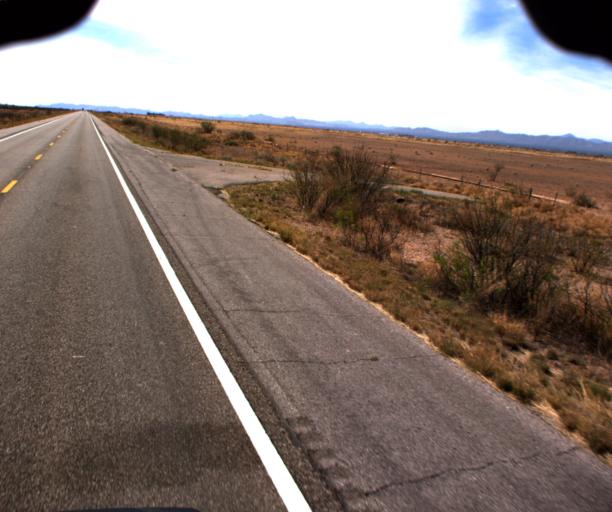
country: US
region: Arizona
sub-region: Cochise County
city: Pirtleville
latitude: 31.5842
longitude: -109.6689
